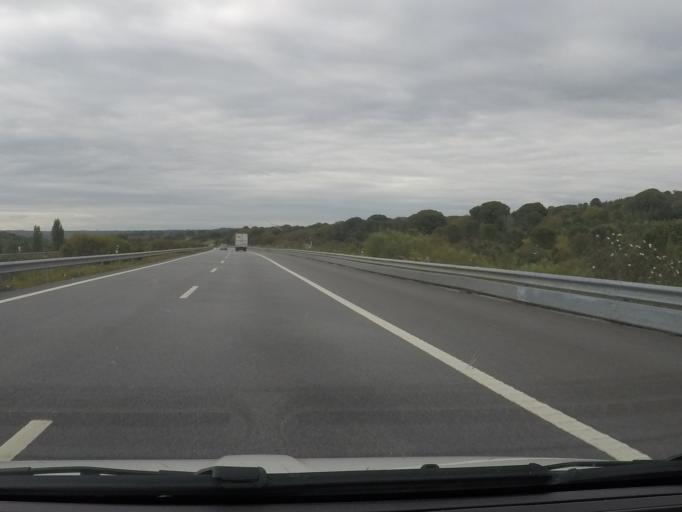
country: PT
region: Setubal
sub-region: Alcacer do Sal
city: Alcacer do Sal
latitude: 38.4769
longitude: -8.5369
